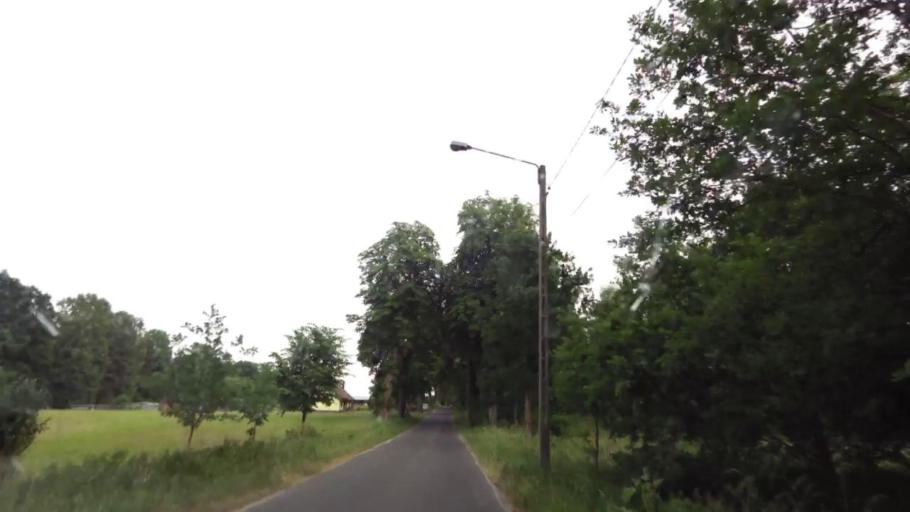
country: PL
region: Pomeranian Voivodeship
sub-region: Powiat bytowski
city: Trzebielino
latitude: 54.2628
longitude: 17.0077
